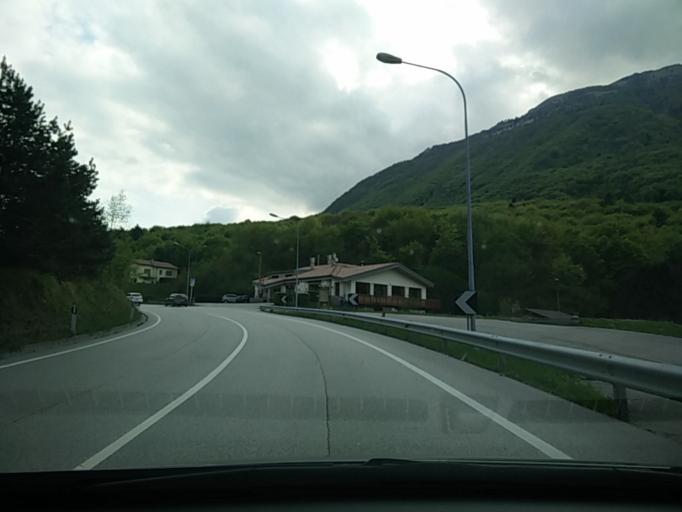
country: IT
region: Veneto
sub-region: Provincia di Belluno
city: Farra d'Alpago
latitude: 46.0845
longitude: 12.3364
